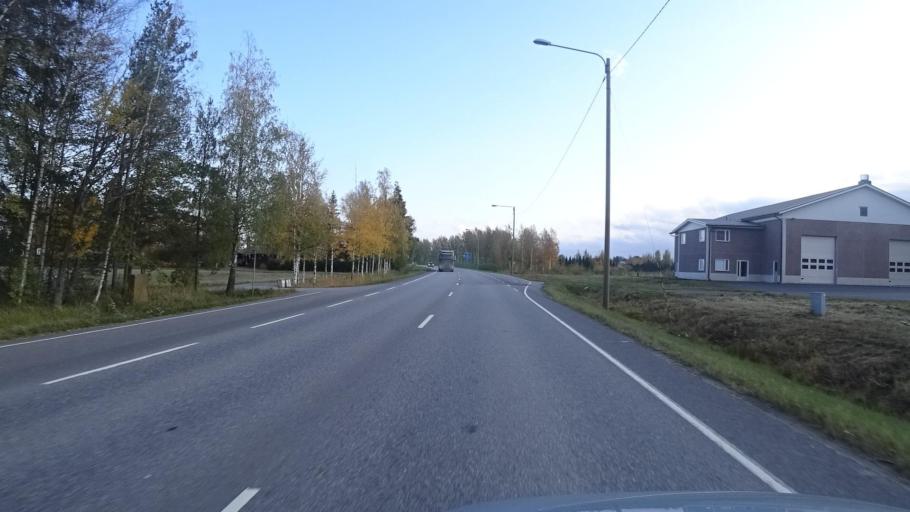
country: FI
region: Satakunta
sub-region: Rauma
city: Saekylae
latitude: 61.0587
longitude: 22.3275
